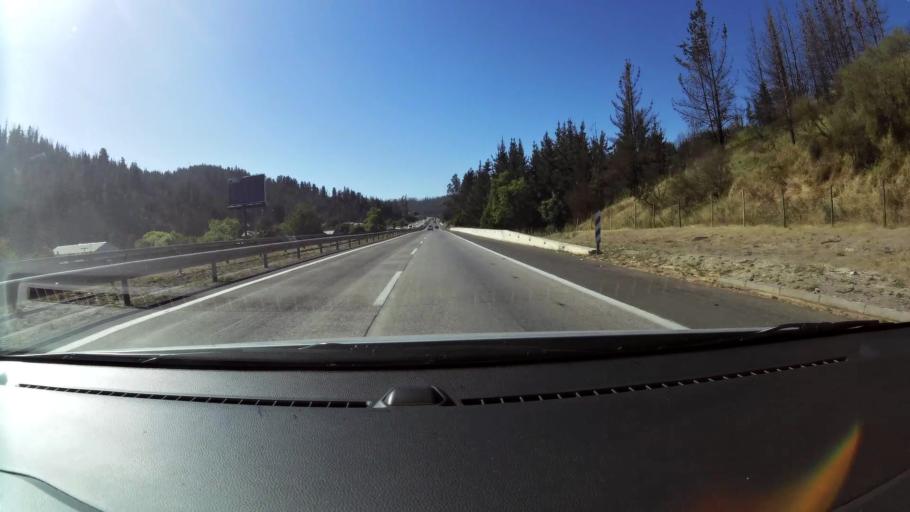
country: CL
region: Valparaiso
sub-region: Provincia de Marga Marga
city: Quilpue
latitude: -33.2265
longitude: -71.4680
